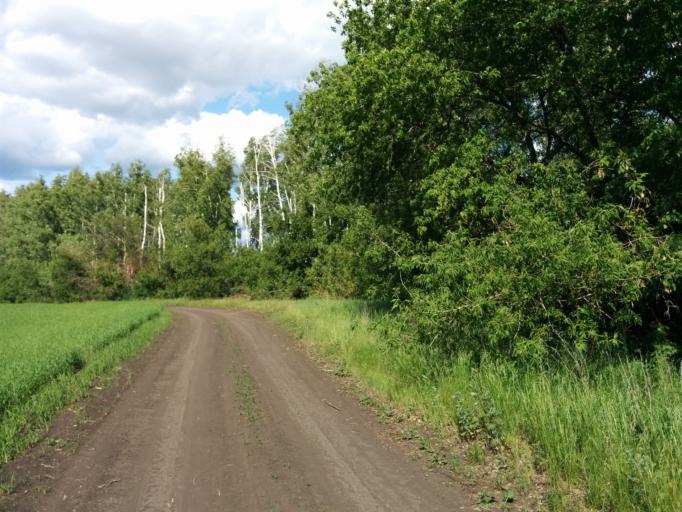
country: RU
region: Tambov
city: Tambov
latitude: 52.7985
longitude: 41.3845
